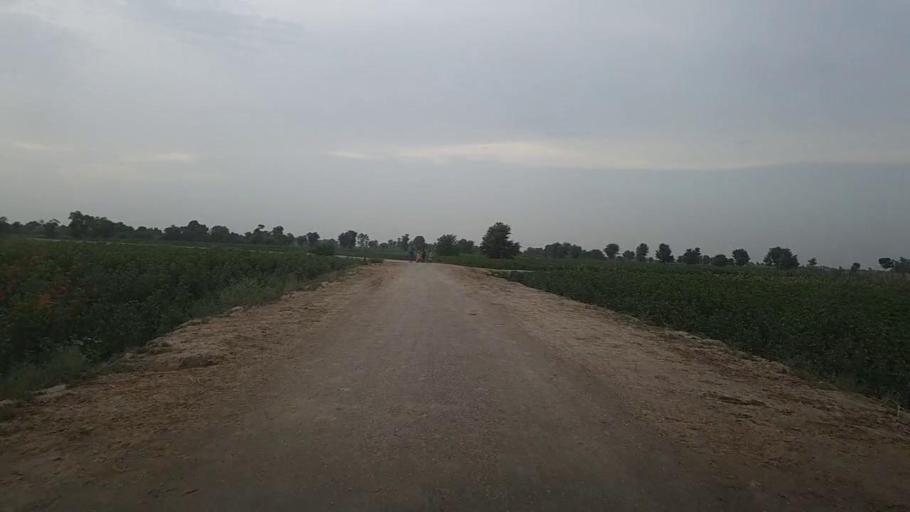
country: PK
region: Sindh
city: Karaundi
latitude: 26.9566
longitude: 68.3626
